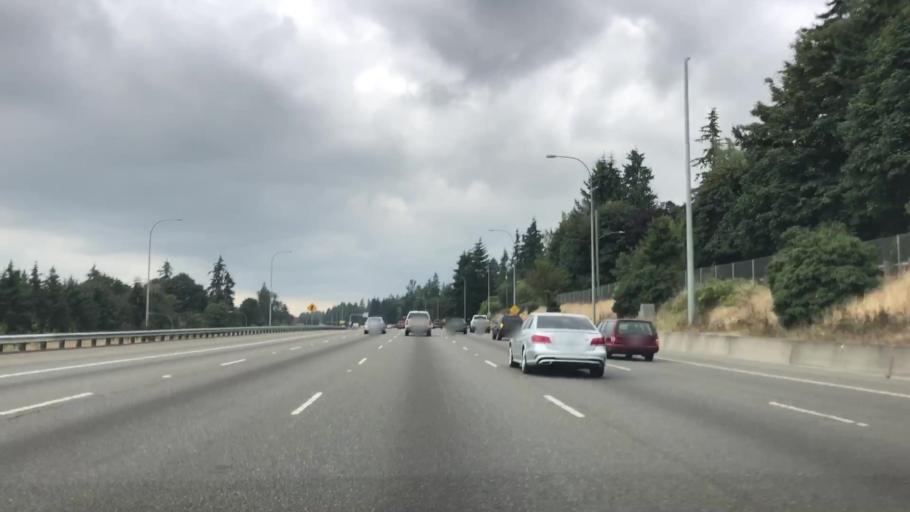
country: US
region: Washington
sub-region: Snohomish County
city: Everett
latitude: 47.9547
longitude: -122.2016
